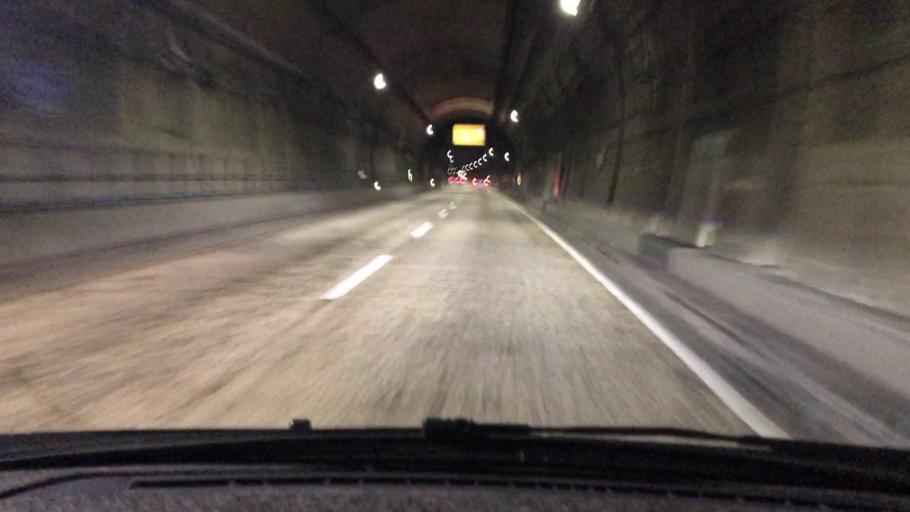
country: JP
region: Hyogo
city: Kobe
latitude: 34.7093
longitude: 135.1920
